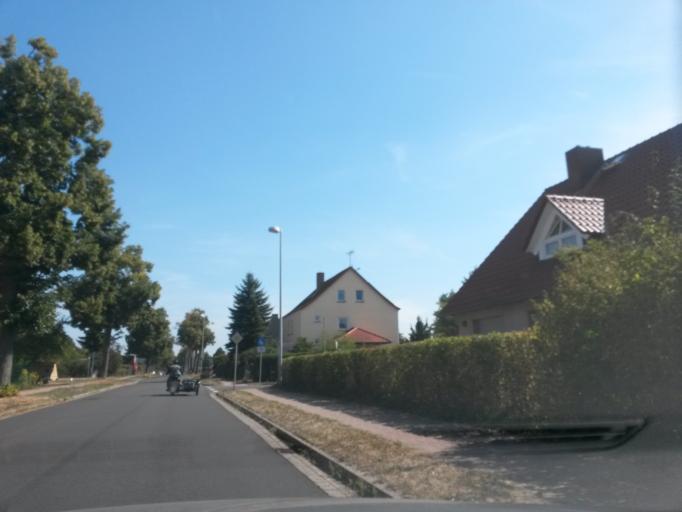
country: DE
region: Brandenburg
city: Wiesenburg
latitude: 52.1155
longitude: 12.4592
